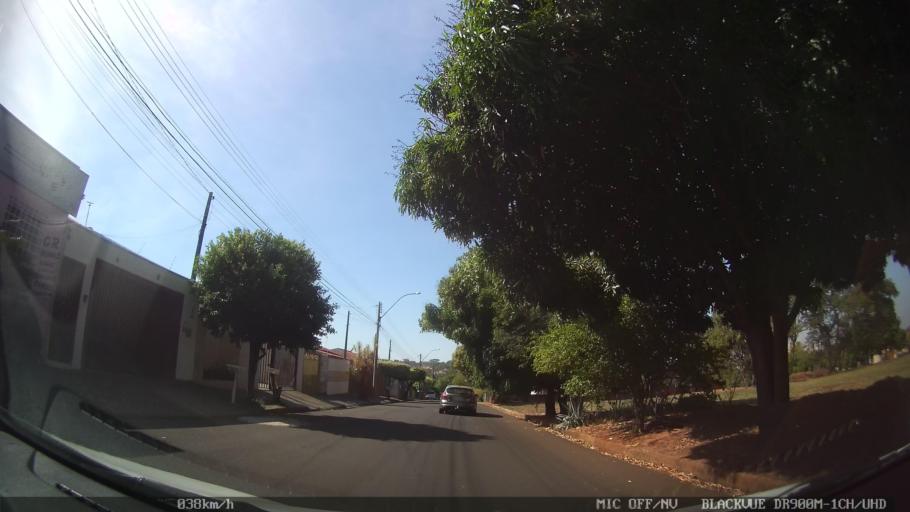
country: BR
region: Sao Paulo
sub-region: Sao Jose Do Rio Preto
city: Sao Jose do Rio Preto
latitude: -20.7882
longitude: -49.4302
